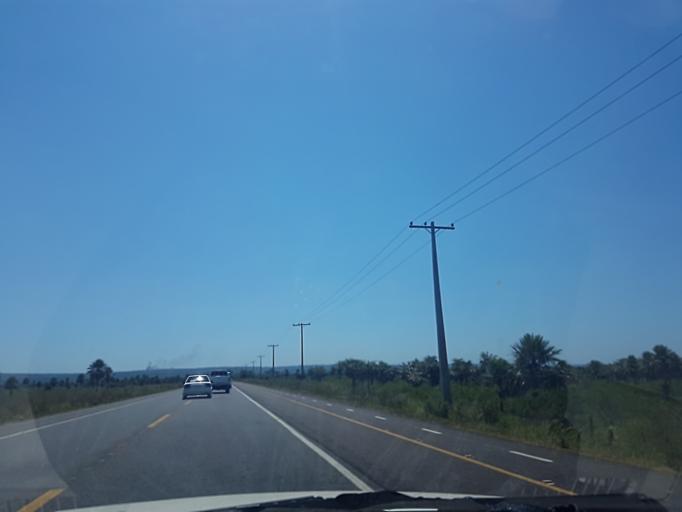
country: PY
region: Cordillera
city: Emboscada
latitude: -25.2092
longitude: -57.4014
